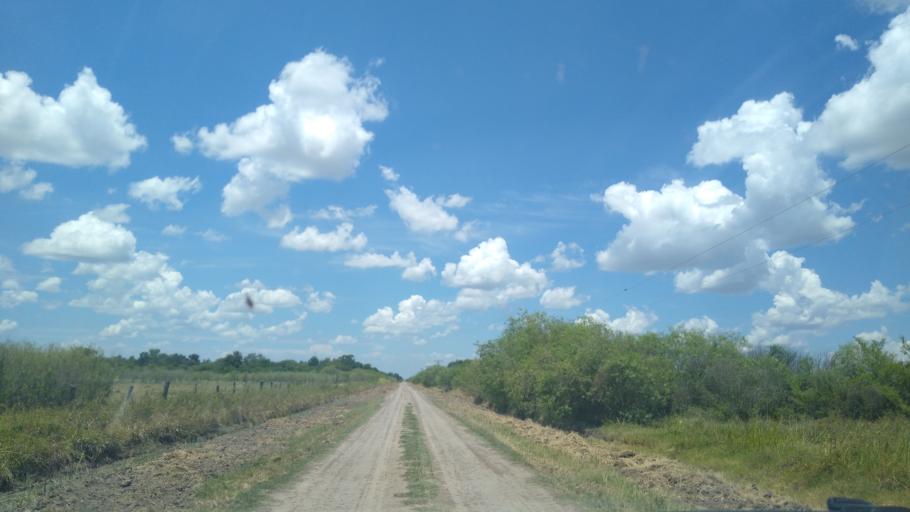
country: AR
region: Chaco
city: Presidencia Roque Saenz Pena
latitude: -26.7370
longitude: -60.3317
